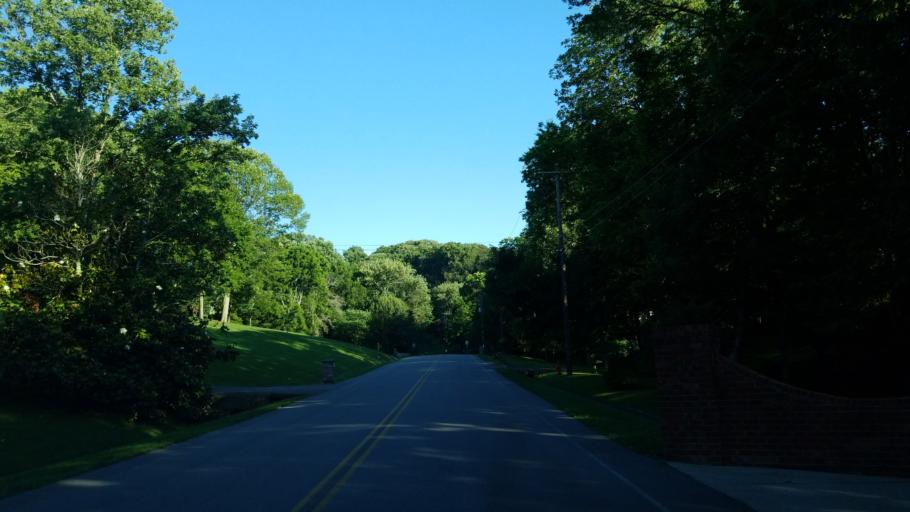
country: US
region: Tennessee
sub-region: Williamson County
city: Brentwood
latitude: 36.0486
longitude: -86.7908
